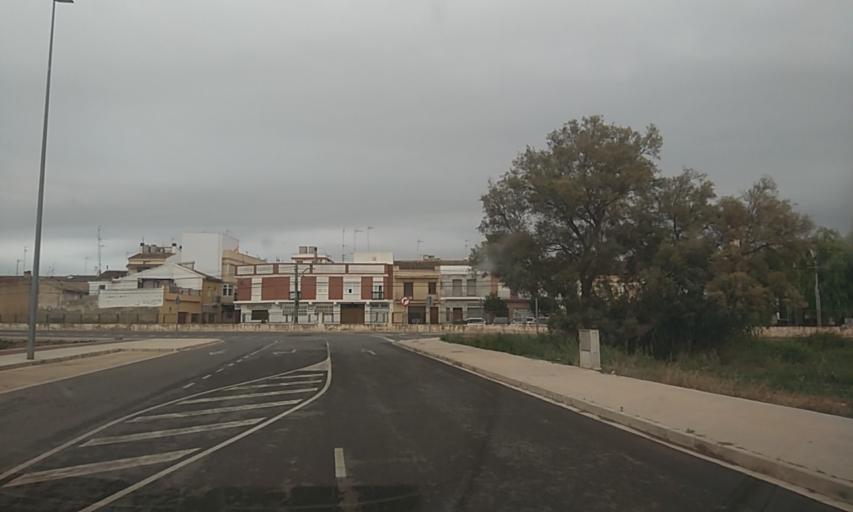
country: ES
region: Valencia
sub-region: Provincia de Valencia
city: L'Alcudia
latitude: 39.1961
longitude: -0.5105
